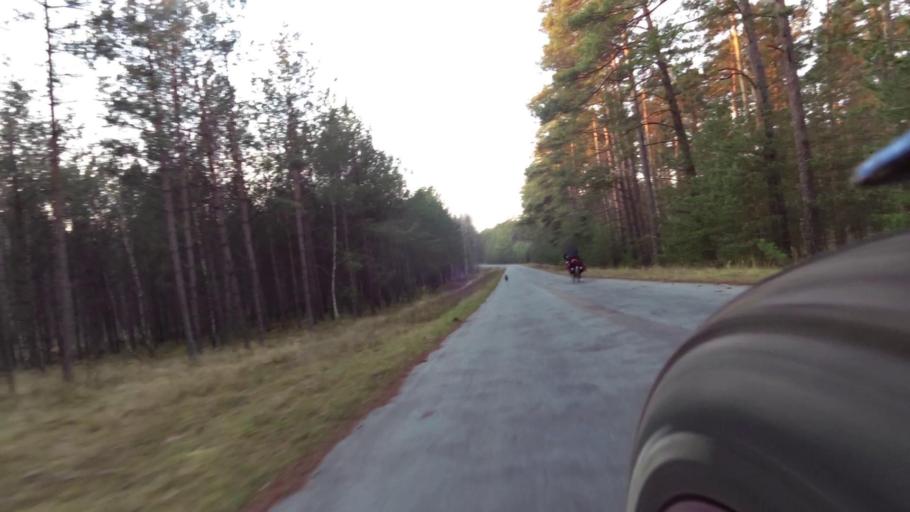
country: PL
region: West Pomeranian Voivodeship
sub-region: Powiat szczecinecki
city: Borne Sulinowo
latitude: 53.5681
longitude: 16.5900
